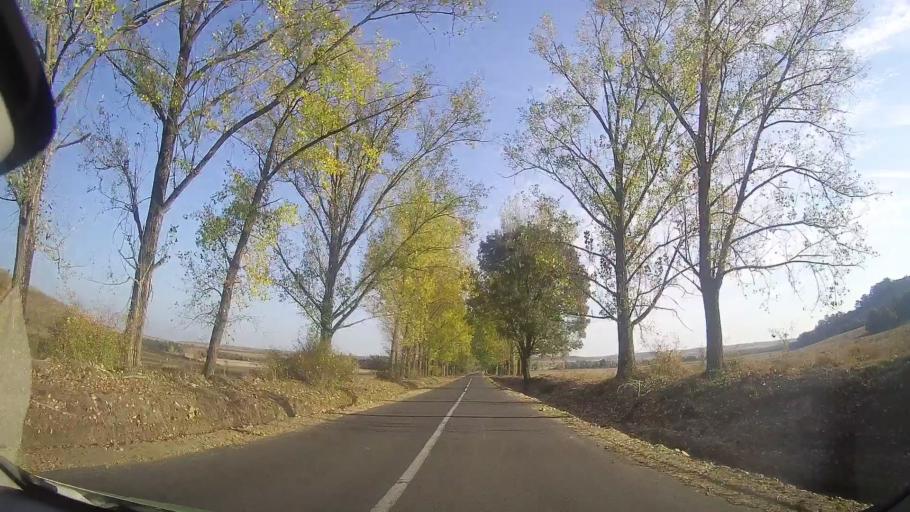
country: RO
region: Timis
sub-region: Comuna Masloc
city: Masloc
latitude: 45.9683
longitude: 21.4919
